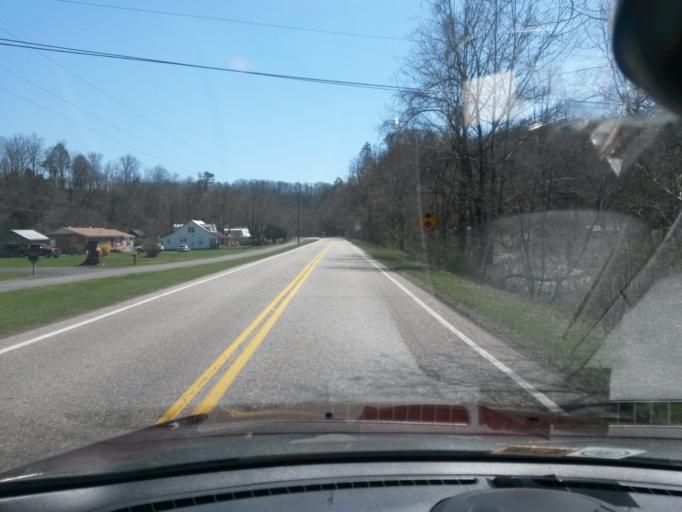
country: US
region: Virginia
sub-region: City of Covington
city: Covington
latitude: 37.8083
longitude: -80.0681
